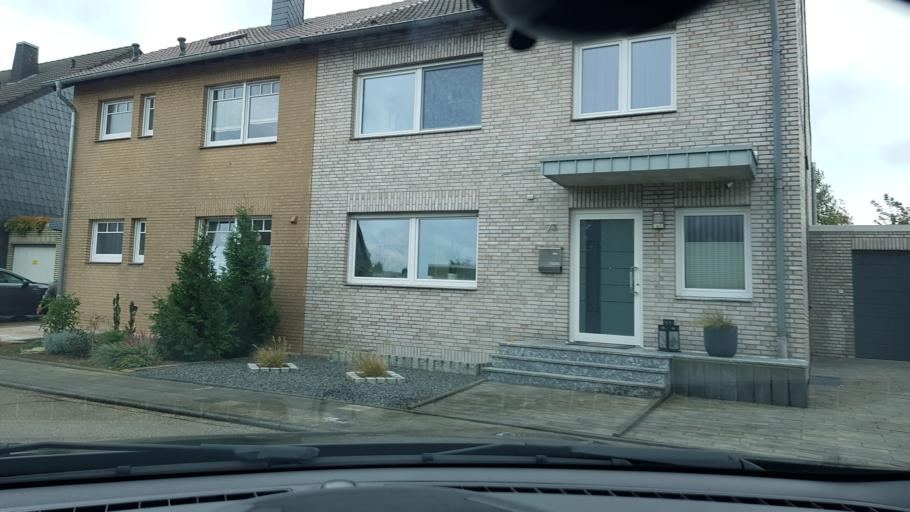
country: DE
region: North Rhine-Westphalia
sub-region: Regierungsbezirk Koln
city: Bedburg
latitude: 51.0005
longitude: 6.5418
